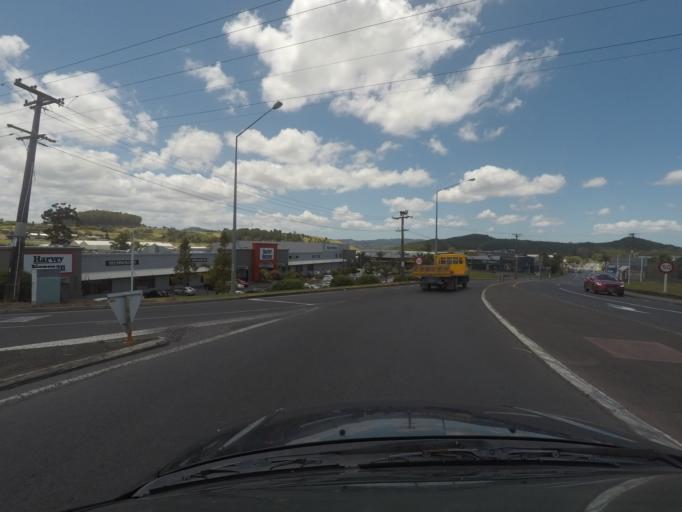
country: NZ
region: Northland
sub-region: Whangarei
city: Whangarei
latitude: -35.7524
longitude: 174.3097
